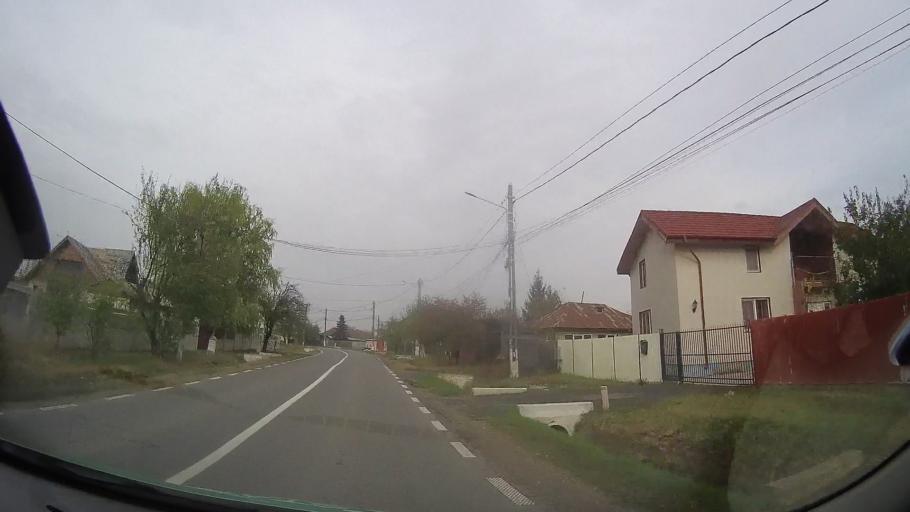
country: RO
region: Ilfov
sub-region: Comuna Gruiu
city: Gruiu
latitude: 44.7231
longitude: 26.2410
